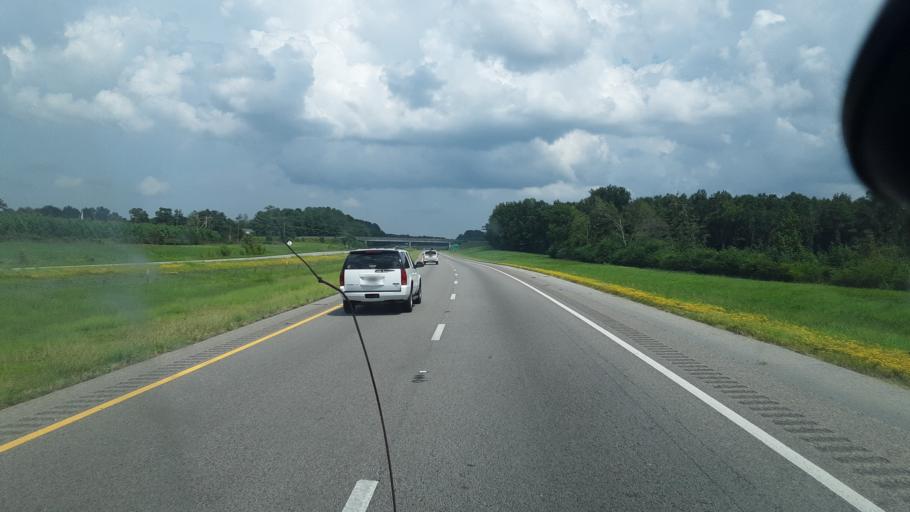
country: US
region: South Carolina
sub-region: Kershaw County
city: Camden
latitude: 34.2135
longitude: -80.5577
